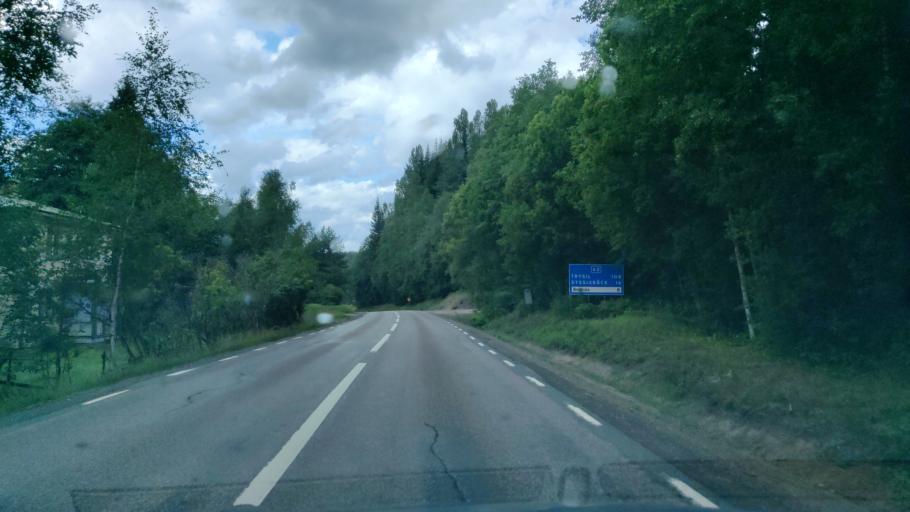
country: SE
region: Vaermland
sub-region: Torsby Kommun
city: Torsby
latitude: 60.6238
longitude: 13.0314
